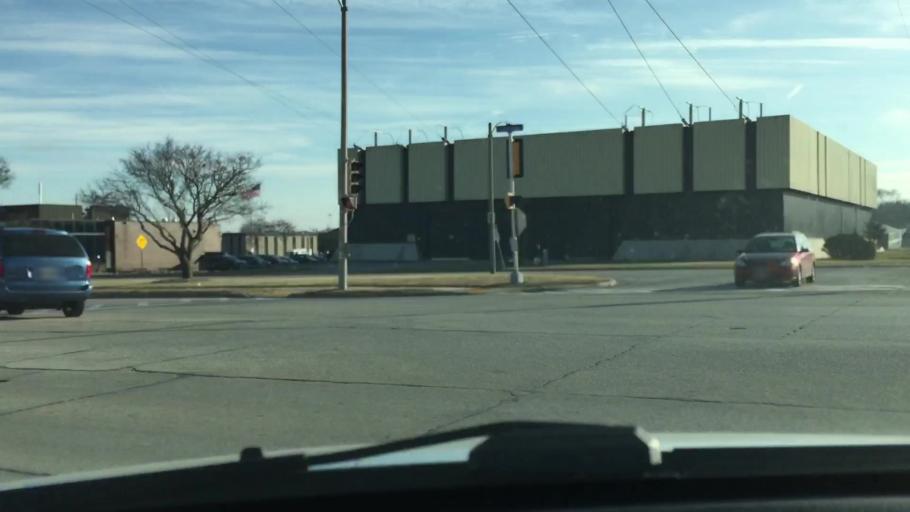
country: US
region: Wisconsin
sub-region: Waukesha County
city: Butler
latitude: 43.0746
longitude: -88.0614
